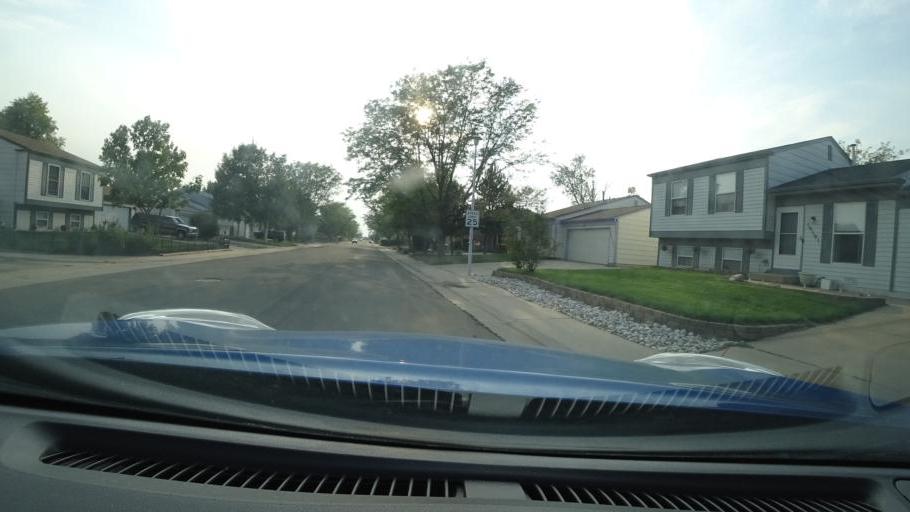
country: US
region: Colorado
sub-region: Adams County
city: Aurora
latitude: 39.7456
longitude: -104.7644
